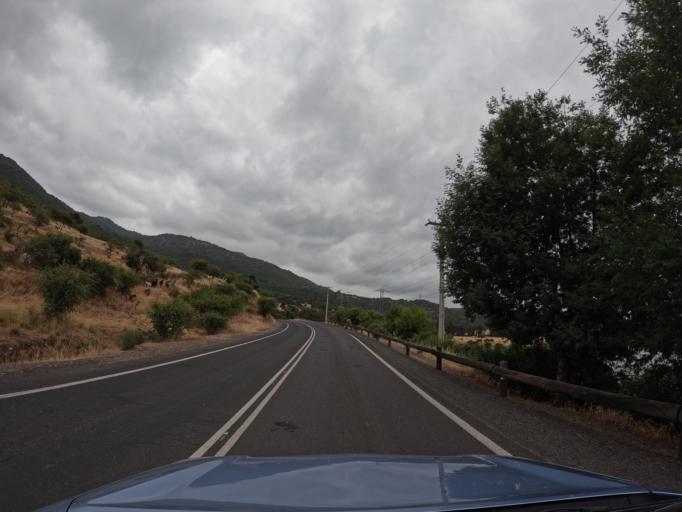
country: CL
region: O'Higgins
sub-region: Provincia de Colchagua
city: Chimbarongo
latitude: -34.7339
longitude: -71.1084
